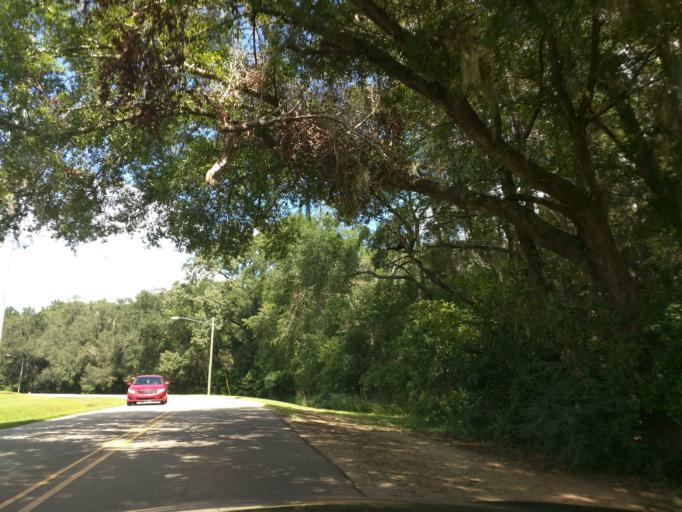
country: US
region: Florida
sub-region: Leon County
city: Tallahassee
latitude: 30.4485
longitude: -84.2159
